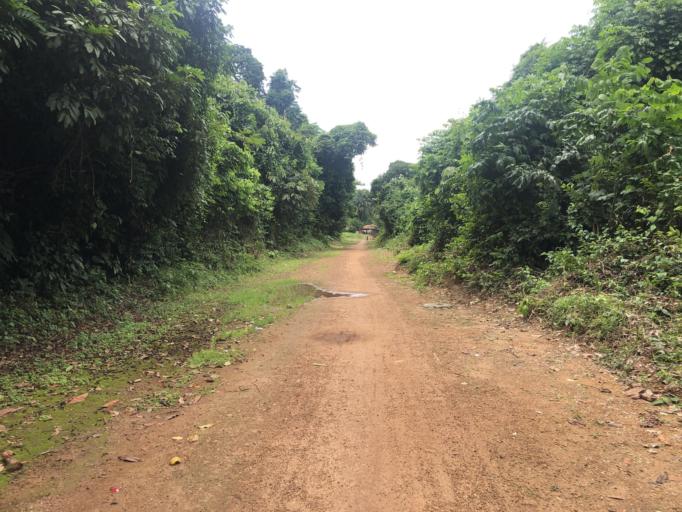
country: SL
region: Northern Province
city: Bumbuna
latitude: 9.0089
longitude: -11.8159
